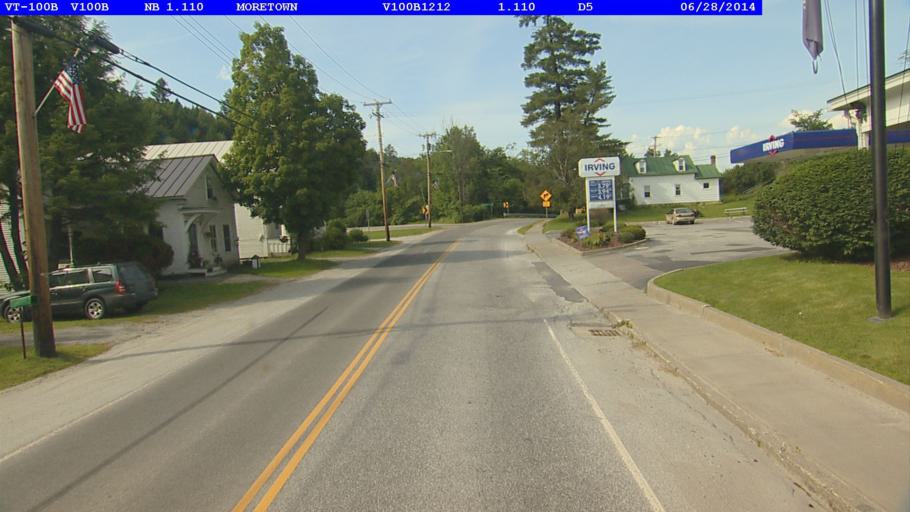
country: US
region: Vermont
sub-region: Washington County
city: Waterbury
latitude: 44.2501
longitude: -72.7614
